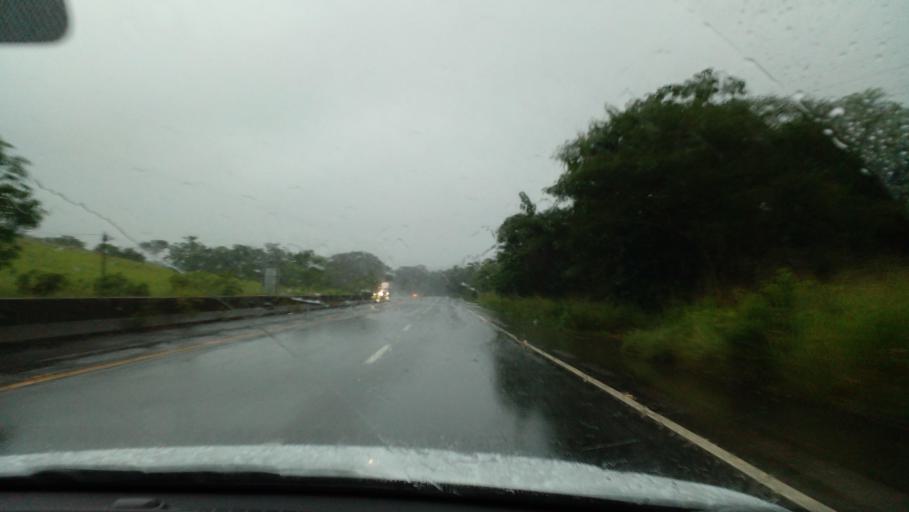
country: PA
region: Chiriqui
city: San Felix
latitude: 8.2947
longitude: -81.9271
